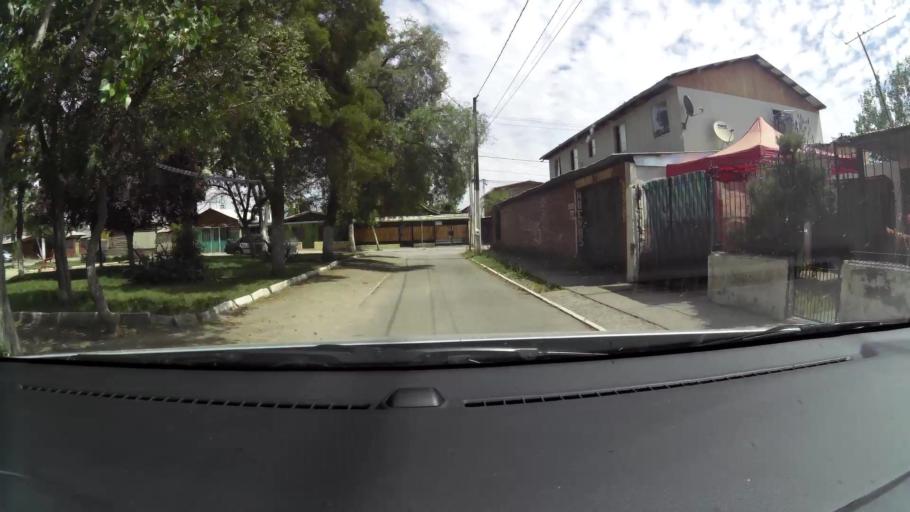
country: CL
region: Santiago Metropolitan
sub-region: Provincia de Santiago
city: La Pintana
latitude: -33.5816
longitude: -70.6541
